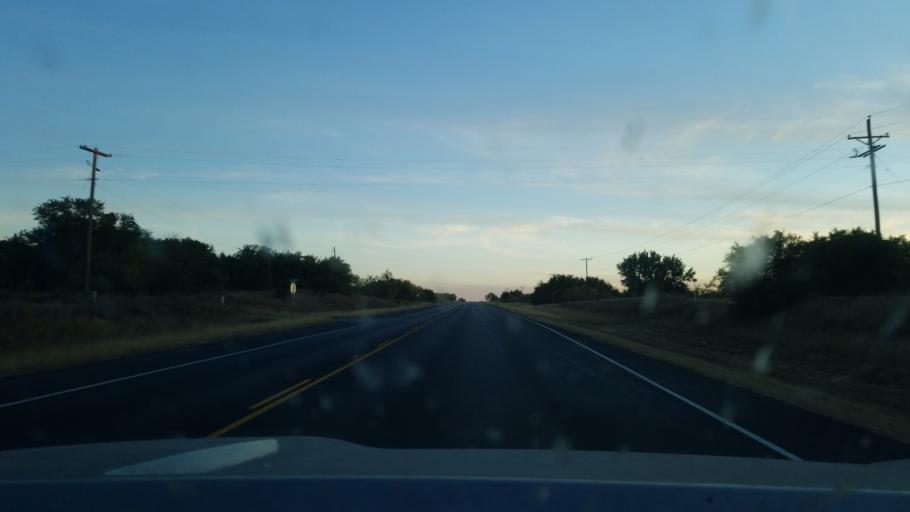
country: US
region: Texas
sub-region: Stephens County
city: Breckenridge
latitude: 32.6888
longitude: -98.9026
